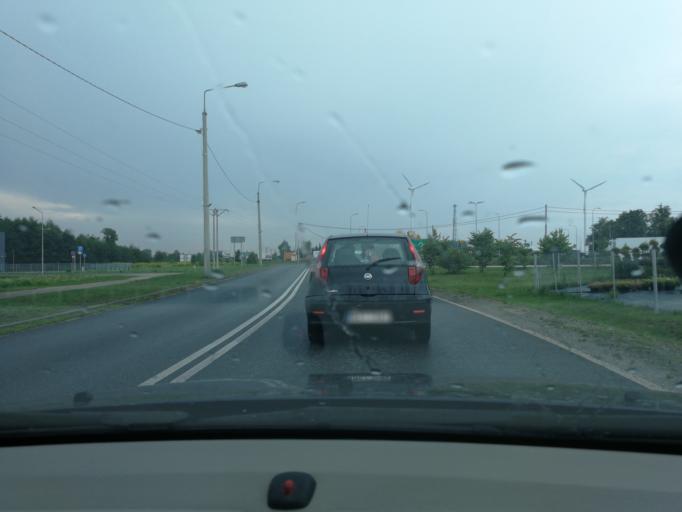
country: PL
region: Masovian Voivodeship
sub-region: Powiat zyrardowski
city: Mszczonow
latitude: 51.9800
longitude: 20.5283
